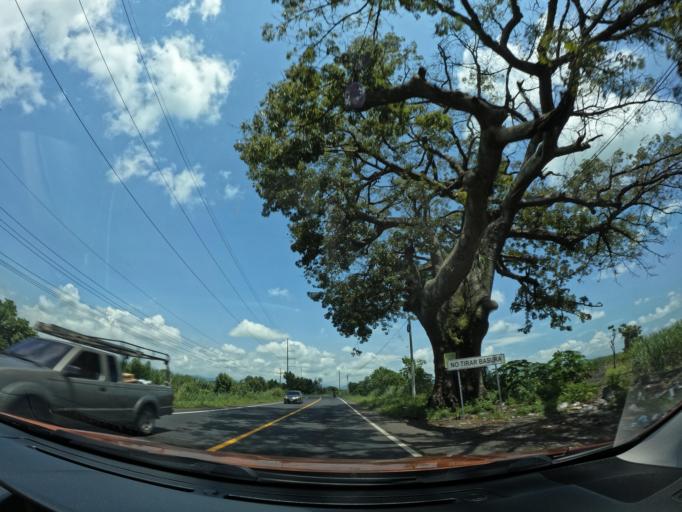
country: GT
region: Escuintla
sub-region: Municipio de Masagua
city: Masagua
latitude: 14.2450
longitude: -90.8115
